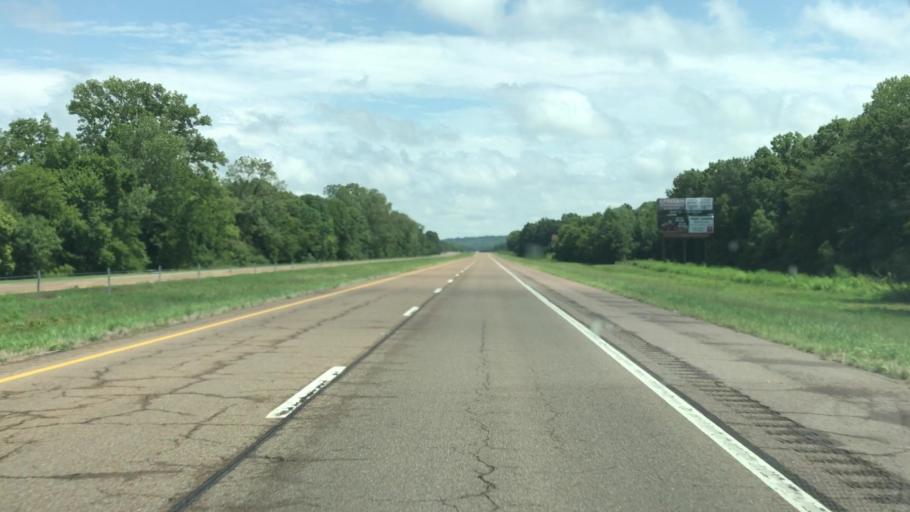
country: US
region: Missouri
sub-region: Pemiscot County
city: Caruthersville
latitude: 36.0828
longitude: -89.5392
